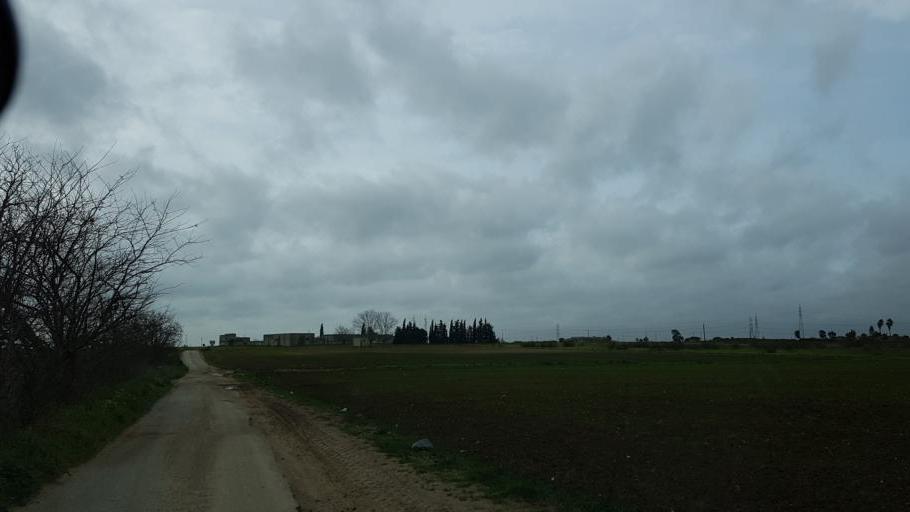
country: IT
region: Apulia
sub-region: Provincia di Brindisi
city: La Rosa
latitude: 40.5944
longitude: 17.9176
